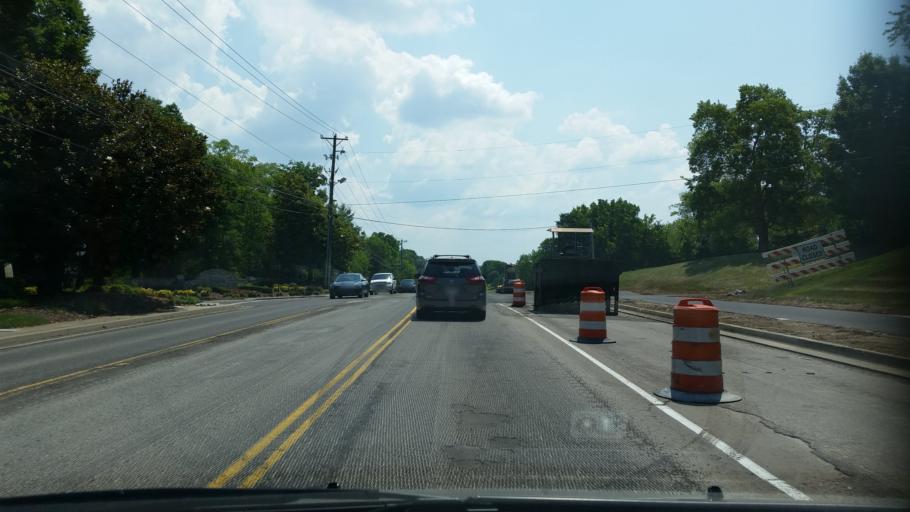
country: US
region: Tennessee
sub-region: Williamson County
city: Brentwood Estates
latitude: 35.9952
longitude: -86.7750
